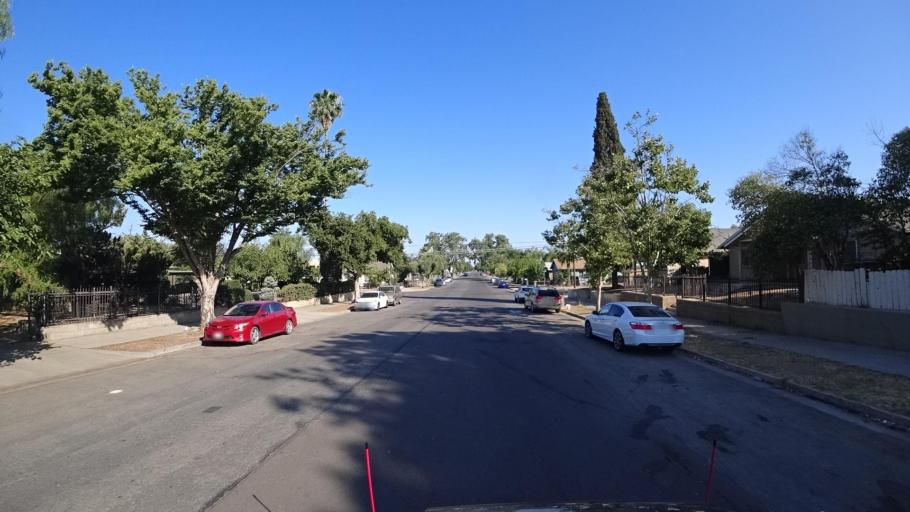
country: US
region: California
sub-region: Fresno County
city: Fresno
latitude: 36.7254
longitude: -119.7985
